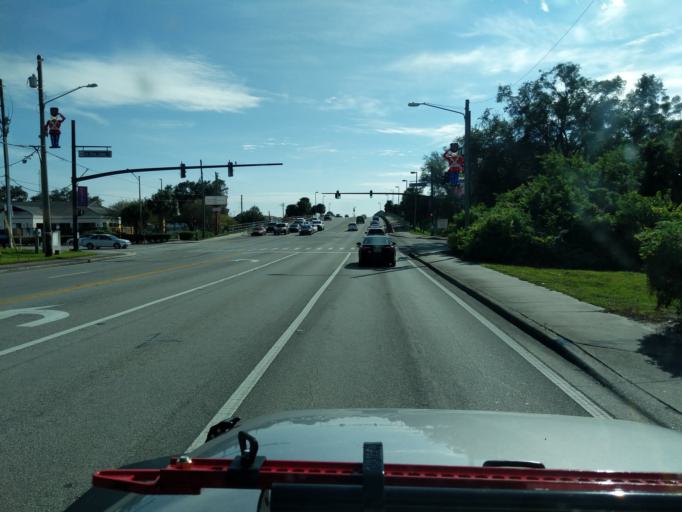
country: US
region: Florida
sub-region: Orange County
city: Ocoee
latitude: 28.5485
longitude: -81.5421
